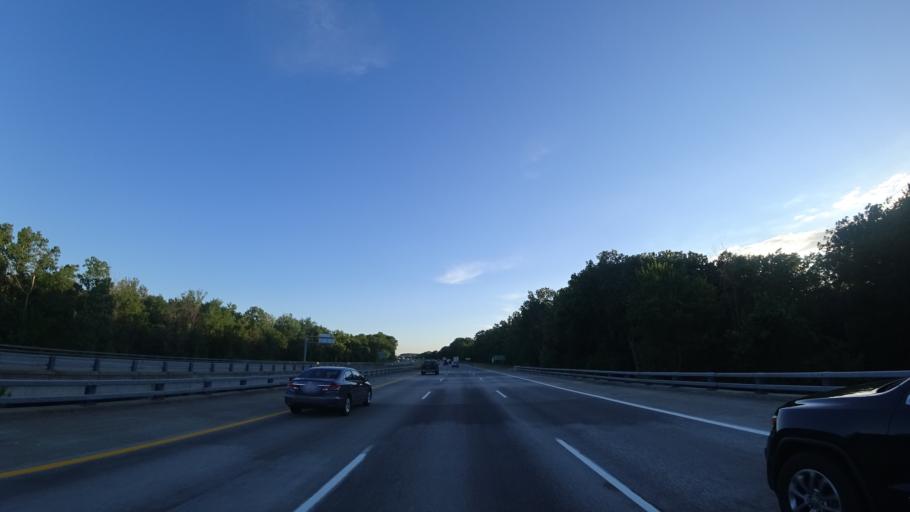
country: US
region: Michigan
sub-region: Berrien County
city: New Buffalo
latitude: 41.8199
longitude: -86.6881
